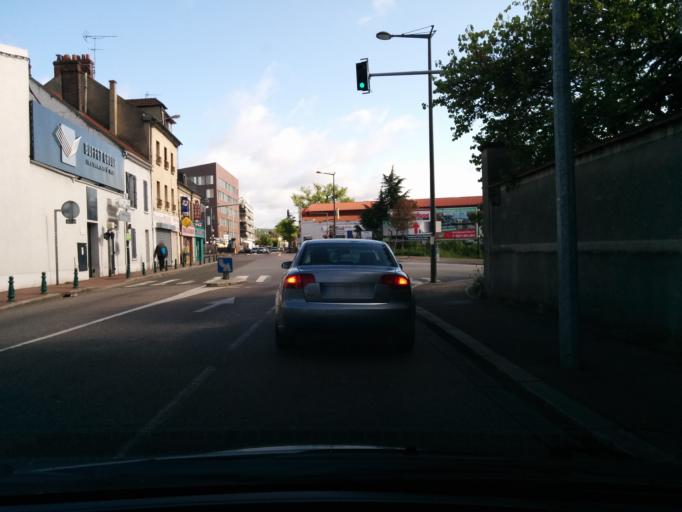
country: FR
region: Ile-de-France
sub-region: Departement des Yvelines
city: Mantes-la-Jolie
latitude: 48.9824
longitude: 1.7163
